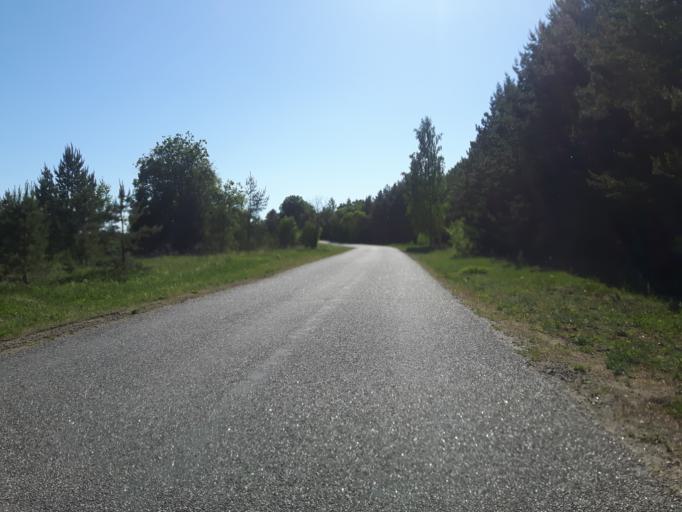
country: EE
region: Laeaene-Virumaa
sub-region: Haljala vald
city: Haljala
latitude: 59.5467
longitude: 26.1192
